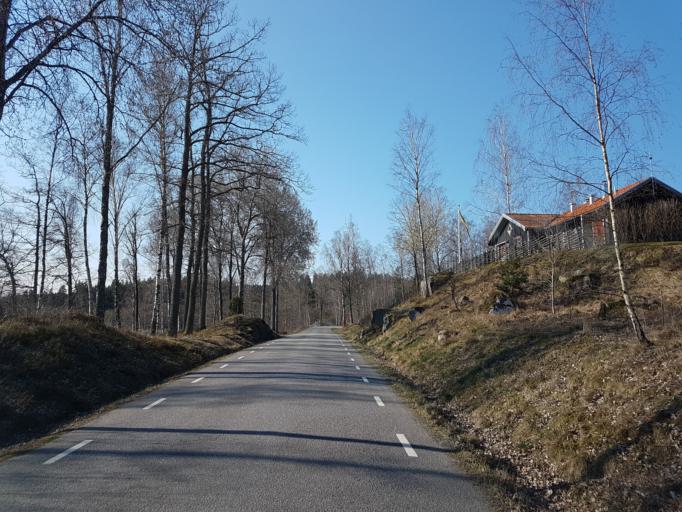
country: SE
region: OEstergoetland
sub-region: Valdemarsviks Kommun
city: Gusum
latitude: 58.1934
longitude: 16.3163
